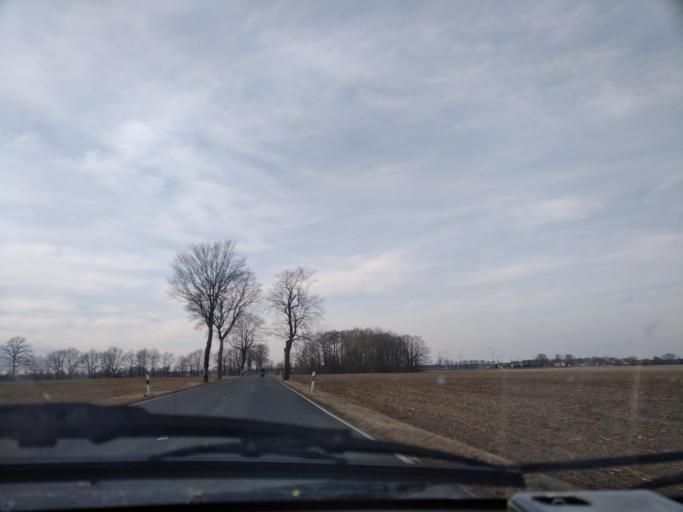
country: DE
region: Saxony-Anhalt
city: Holzdorf
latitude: 51.8085
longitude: 13.1674
